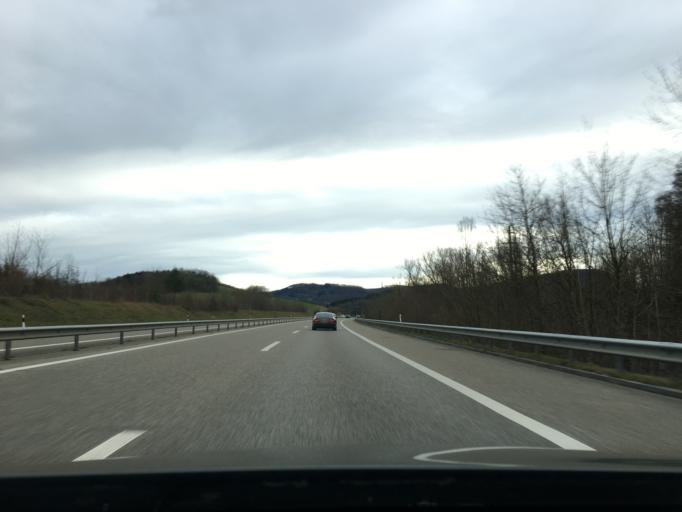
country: CH
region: Aargau
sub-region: Bezirk Laufenburg
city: Sulz
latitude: 47.4948
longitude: 8.0798
